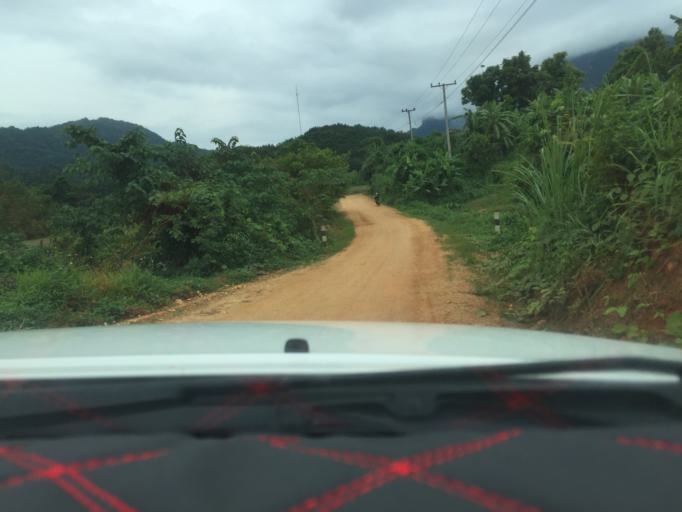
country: TH
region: Phayao
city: Phu Sang
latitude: 19.7712
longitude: 100.5221
